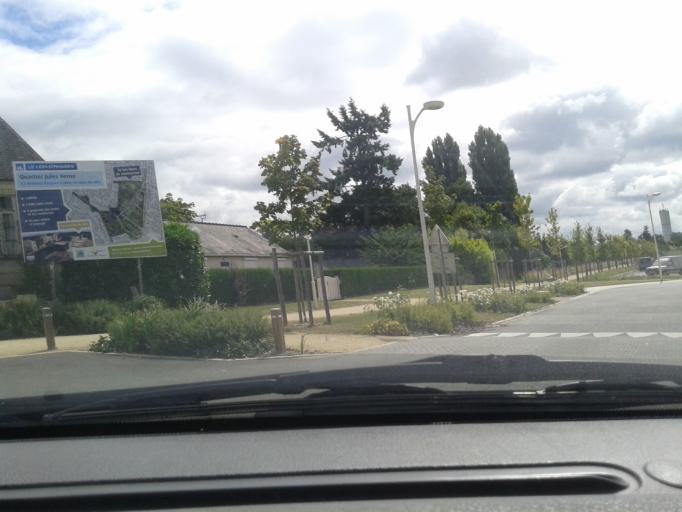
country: FR
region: Pays de la Loire
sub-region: Departement de Maine-et-Loire
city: Grez-Neuville
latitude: 47.6239
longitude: -0.7176
